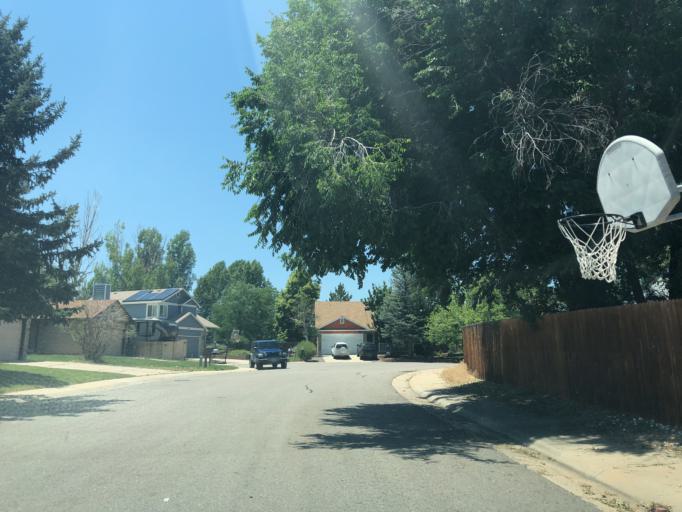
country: US
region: Colorado
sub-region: Arapahoe County
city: Dove Valley
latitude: 39.6245
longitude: -104.7577
